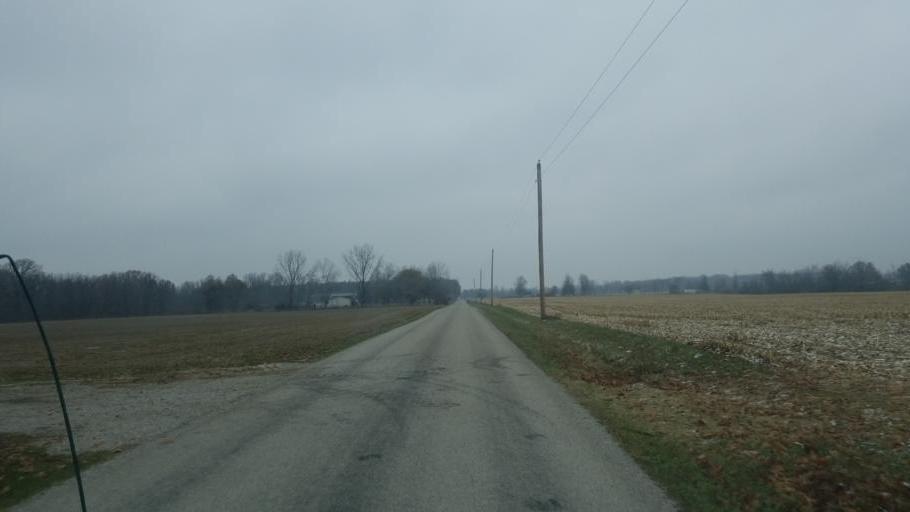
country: US
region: Ohio
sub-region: Huron County
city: New London
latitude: 41.0231
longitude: -82.3257
